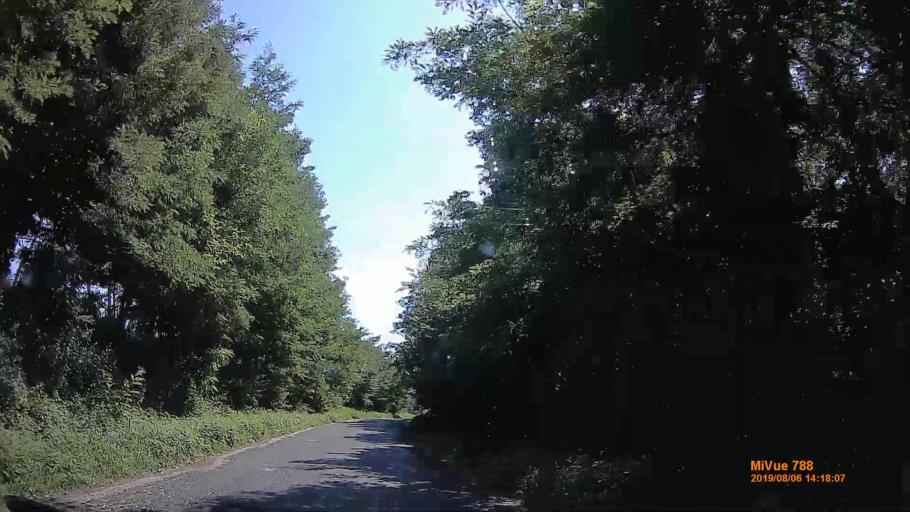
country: HU
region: Zala
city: Zalakomar
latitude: 46.5383
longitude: 17.0829
